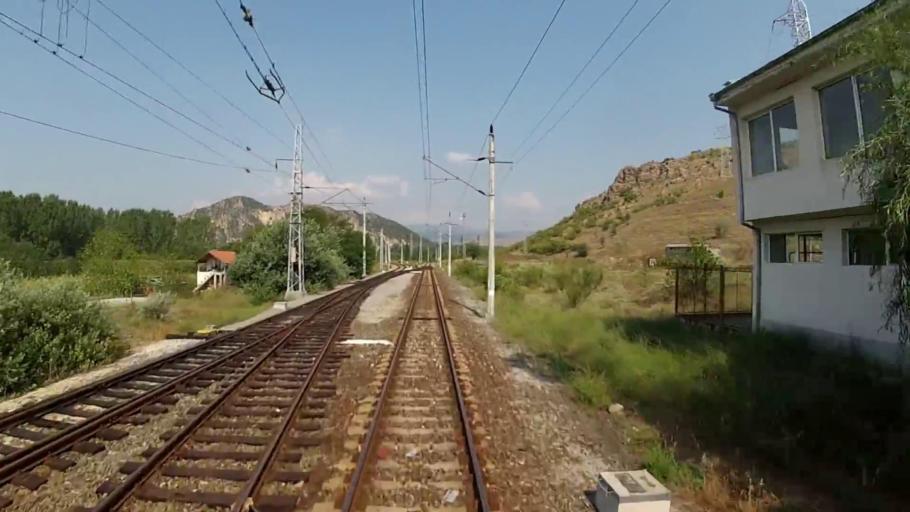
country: BG
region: Blagoevgrad
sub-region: Obshtina Petrich
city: Petrich
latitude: 41.4624
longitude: 23.2704
